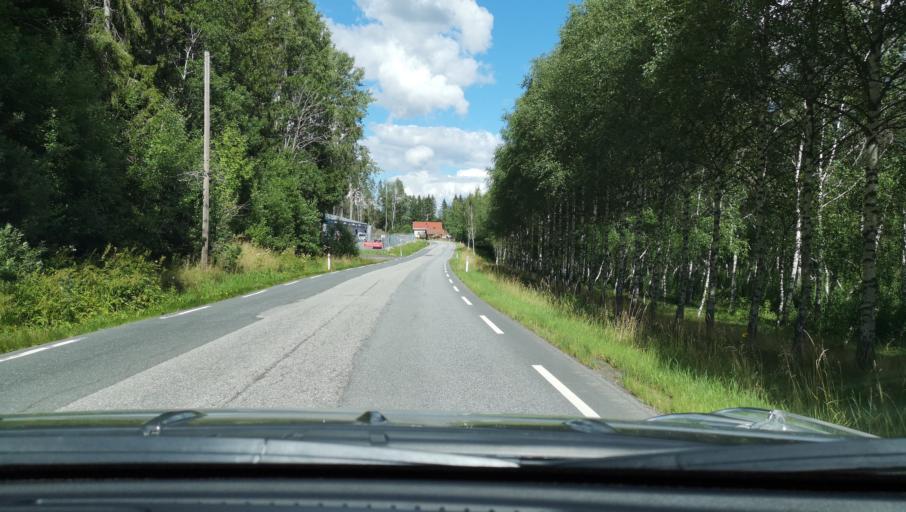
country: NO
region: Ostfold
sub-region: Hobol
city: Elvestad
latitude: 59.6368
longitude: 10.9636
